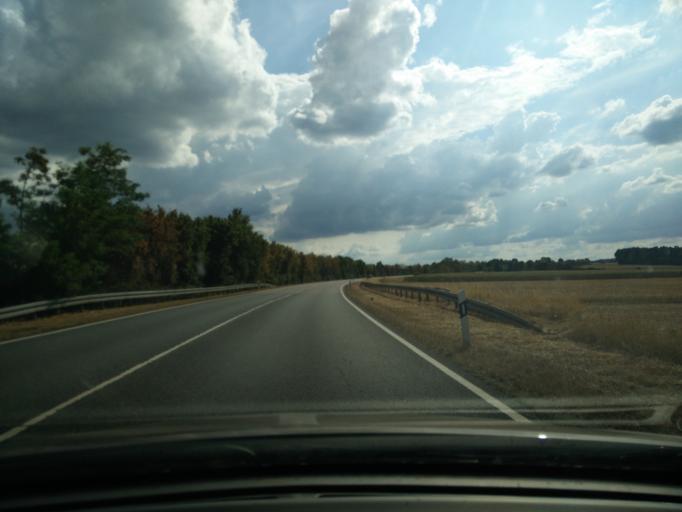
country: DE
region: Bavaria
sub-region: Regierungsbezirk Mittelfranken
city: Stein
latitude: 49.4021
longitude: 10.9967
